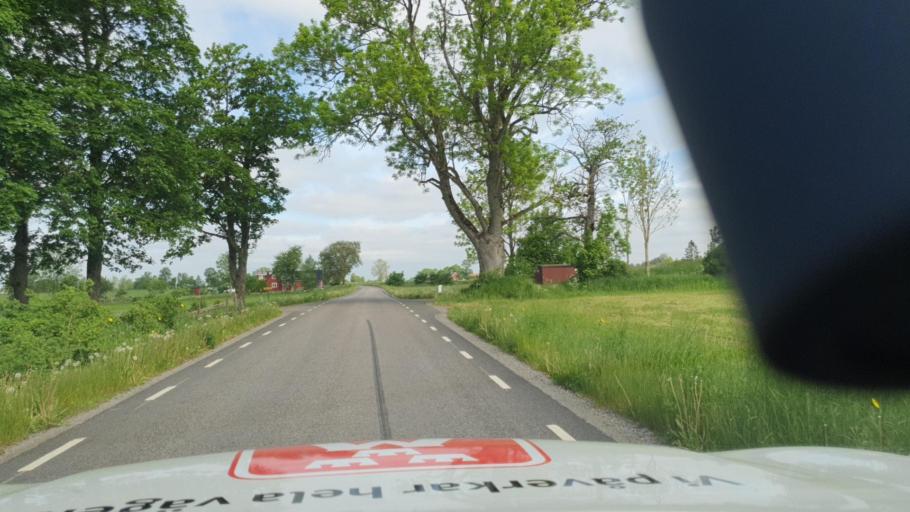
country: SE
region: Vaestra Goetaland
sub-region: Falkopings Kommun
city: Floby
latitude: 58.1595
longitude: 13.4245
